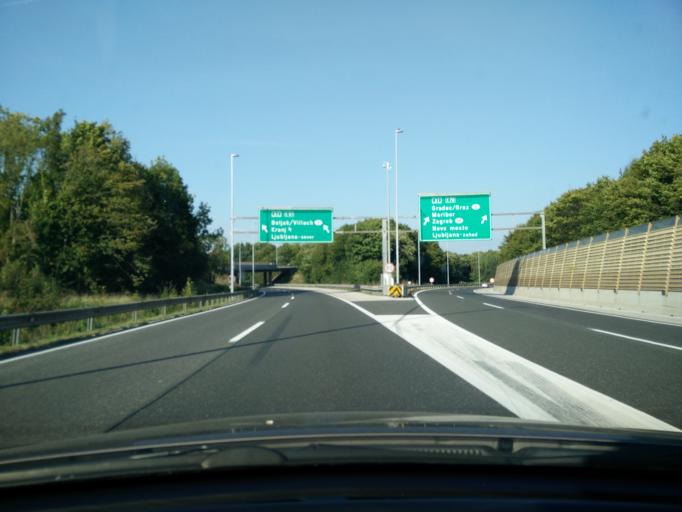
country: SI
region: Brezovica
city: Vnanje Gorice
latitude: 46.0354
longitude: 14.4487
